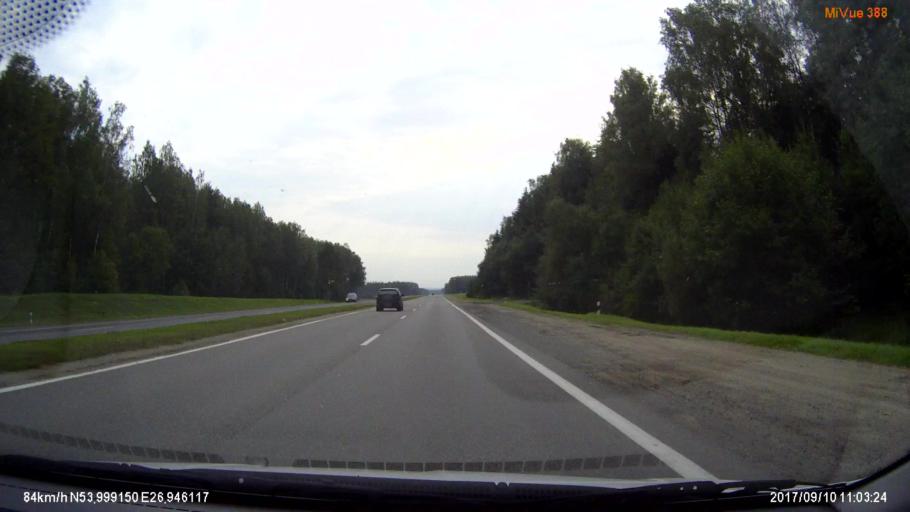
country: BY
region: Minsk
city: Rakaw
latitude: 53.9991
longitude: 26.9461
